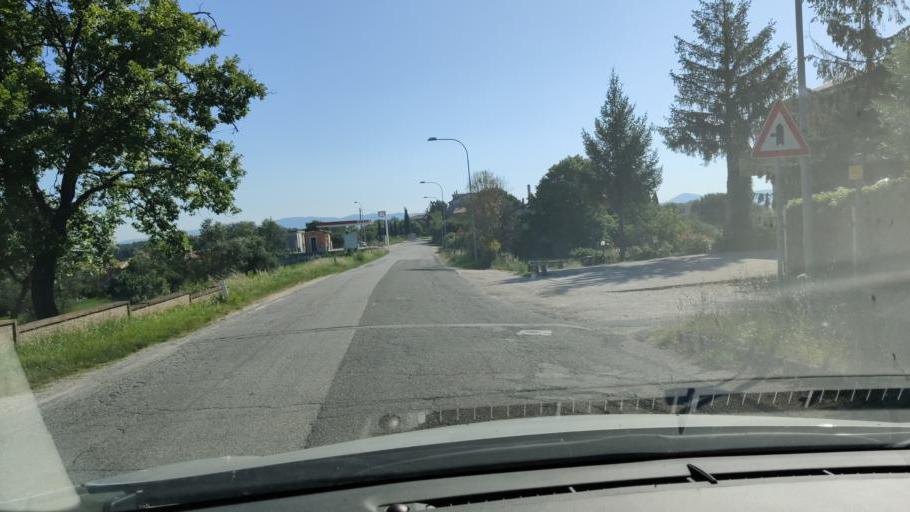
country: IT
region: Umbria
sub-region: Provincia di Terni
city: Avigliano Umbro
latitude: 42.6579
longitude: 12.4320
